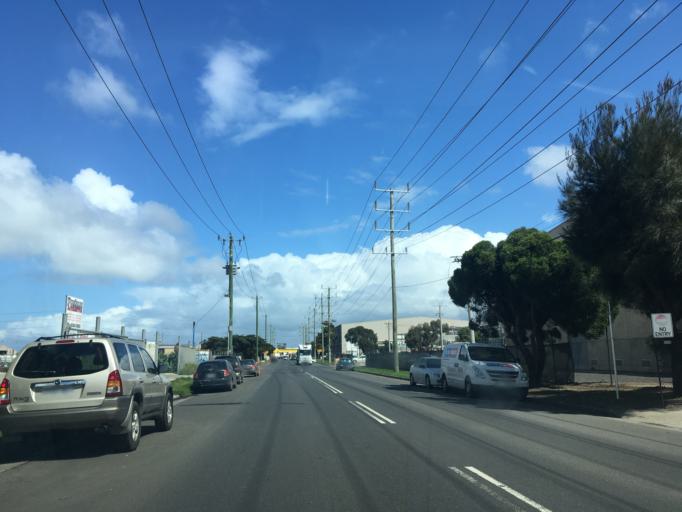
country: AU
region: Victoria
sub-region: Brimbank
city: Sunshine West
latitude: -37.8259
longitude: 144.7968
